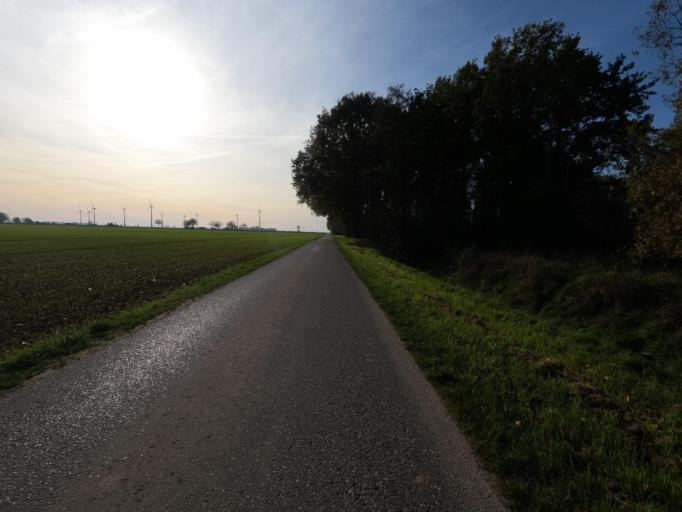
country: DE
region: North Rhine-Westphalia
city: Erkelenz
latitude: 51.0610
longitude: 6.3752
